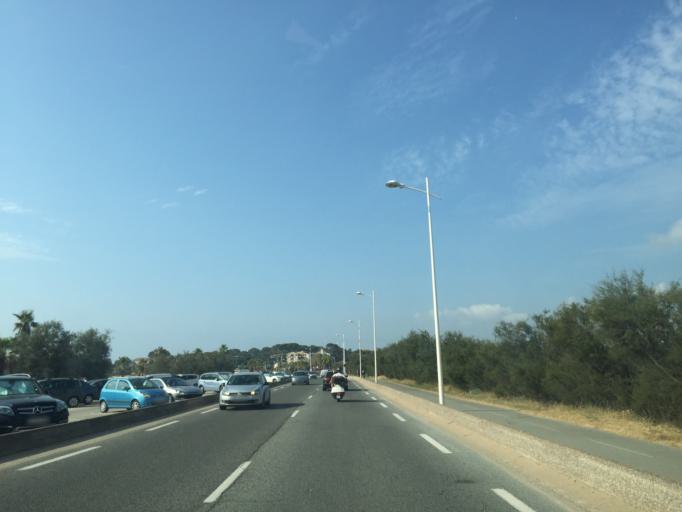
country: FR
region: Provence-Alpes-Cote d'Azur
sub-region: Departement du Var
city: Frejus
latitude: 43.3967
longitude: 6.7289
